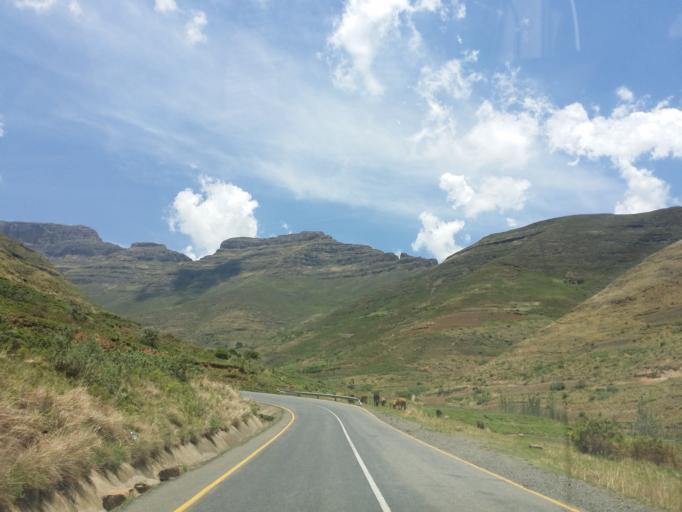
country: LS
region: Butha-Buthe
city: Butha-Buthe
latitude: -28.7634
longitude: 28.5495
